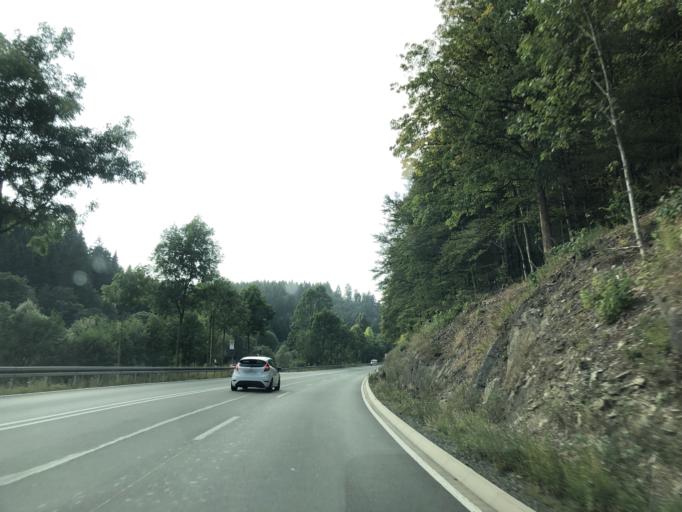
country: DE
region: North Rhine-Westphalia
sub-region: Regierungsbezirk Arnsberg
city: Winterberg
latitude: 51.1781
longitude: 8.5297
